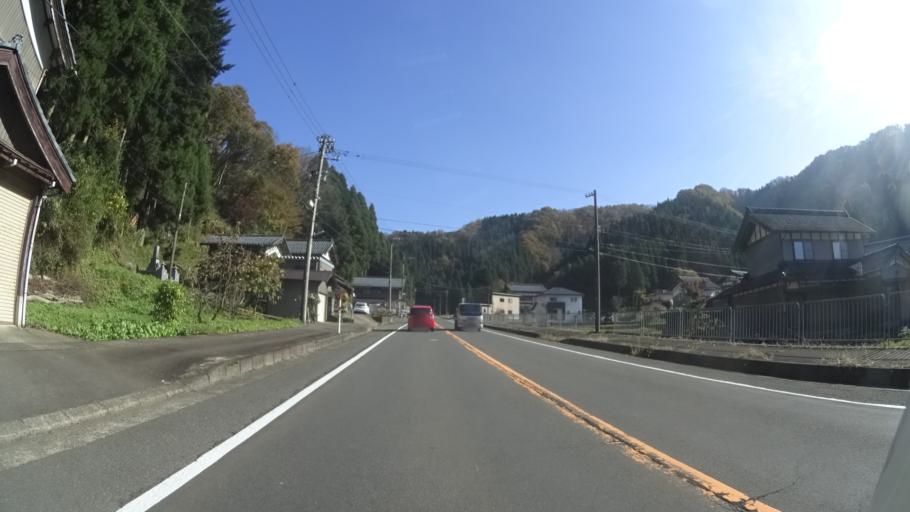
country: JP
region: Fukui
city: Ono
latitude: 35.9931
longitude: 136.4476
